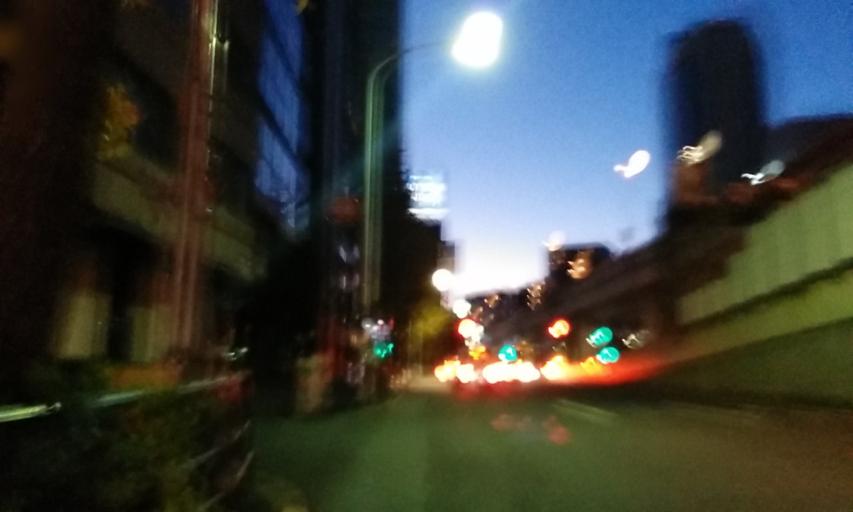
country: JP
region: Tokyo
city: Tokyo
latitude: 35.6593
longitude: 139.7209
